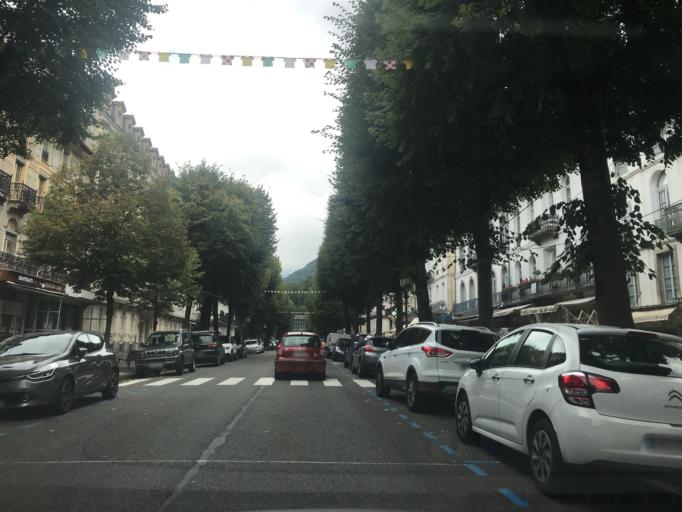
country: FR
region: Midi-Pyrenees
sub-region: Departement de la Haute-Garonne
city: Bagneres-de-Luchon
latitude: 42.7875
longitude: 0.5930
